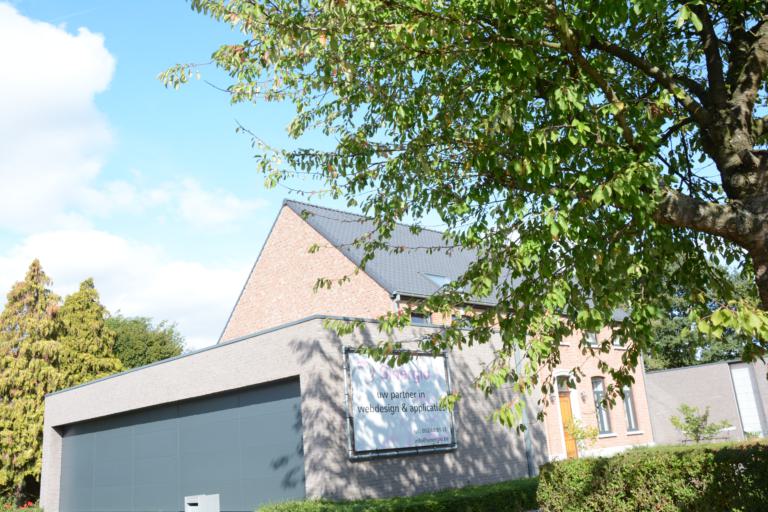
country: BE
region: Flanders
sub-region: Provincie Oost-Vlaanderen
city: Buggenhout
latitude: 51.0202
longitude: 4.2147
